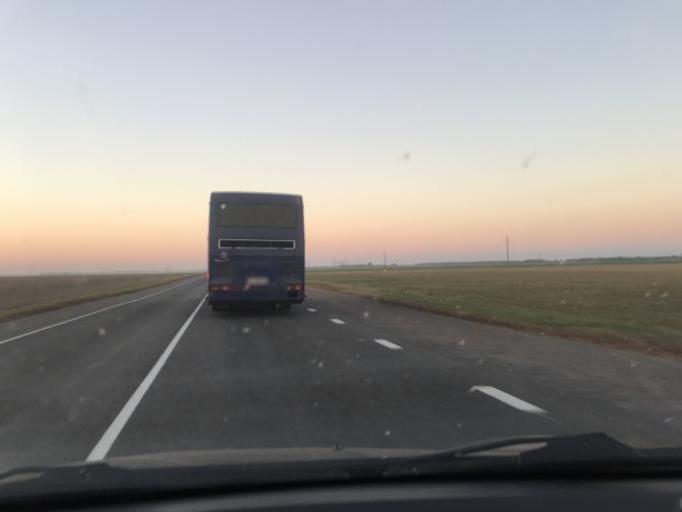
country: BY
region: Gomel
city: Horad Rechytsa
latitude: 52.2248
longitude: 30.5171
